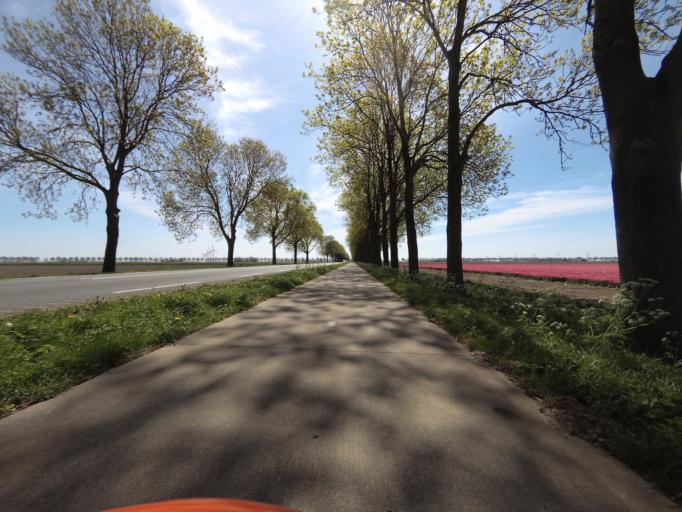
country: NL
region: Flevoland
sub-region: Gemeente Dronten
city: Biddinghuizen
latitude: 52.4915
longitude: 5.6537
